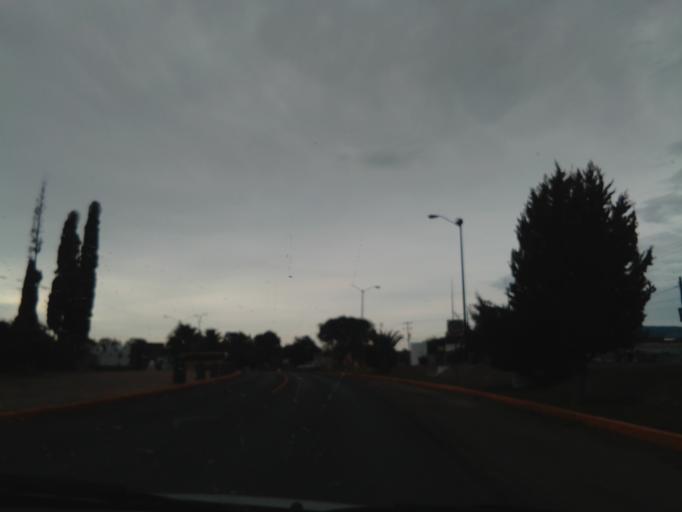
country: MX
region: Guanajuato
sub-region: Dolores Hidalgo Cuna de la Independencia Nacional
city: Dolores Hidalgo Cuna de la Independencia Nacional
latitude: 21.1579
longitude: -100.9166
